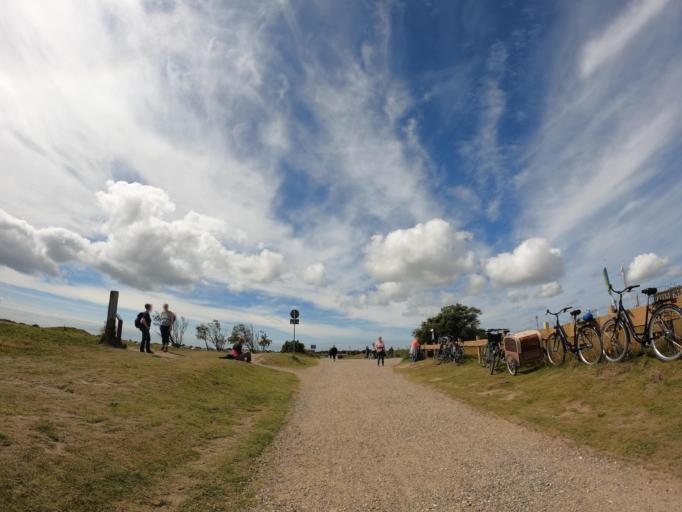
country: DE
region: Schleswig-Holstein
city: Sylt-Ost
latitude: 54.8732
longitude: 8.4599
